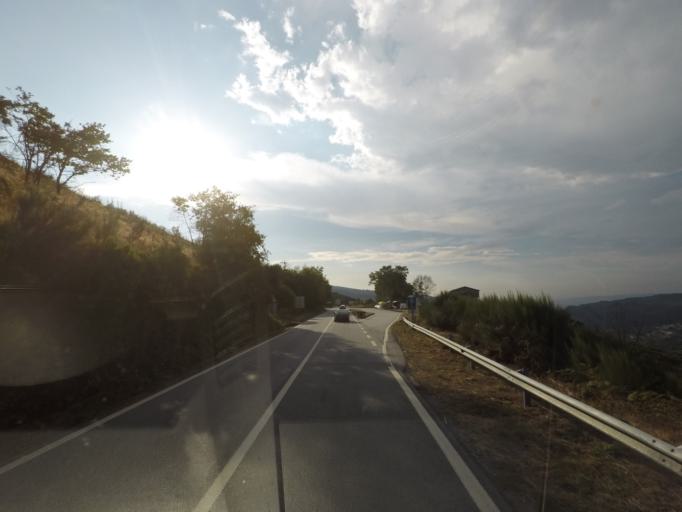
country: PT
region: Porto
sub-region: Baiao
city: Valadares
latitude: 41.2020
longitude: -7.9588
